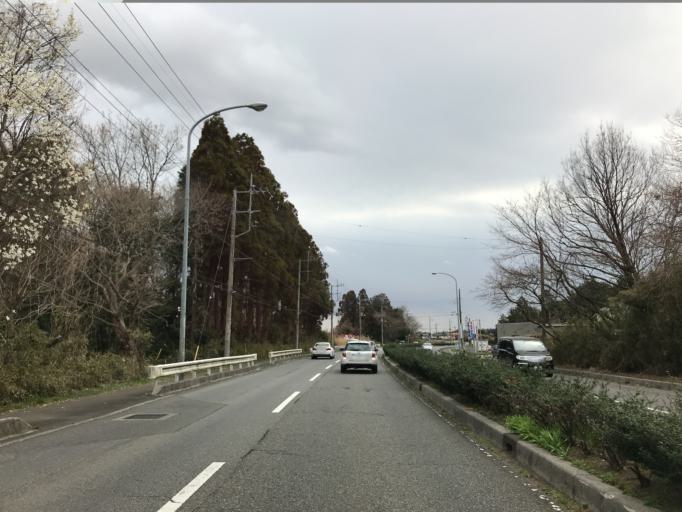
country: JP
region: Ibaraki
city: Ushiku
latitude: 36.0110
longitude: 140.0840
